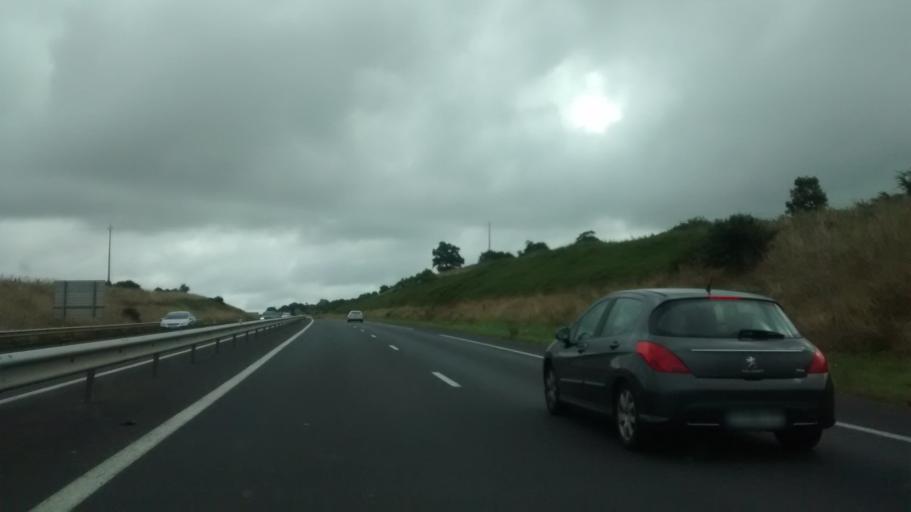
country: FR
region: Lower Normandy
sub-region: Departement de la Manche
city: Saint-Amand
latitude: 48.9916
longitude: -0.9228
